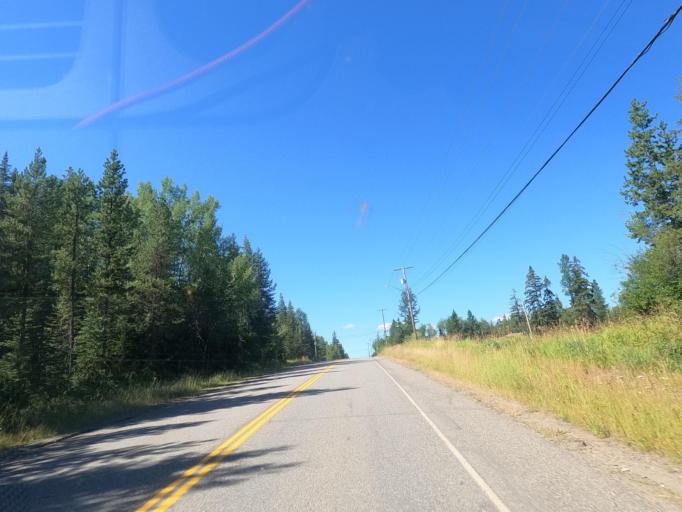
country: CA
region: British Columbia
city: Quesnel
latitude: 53.0293
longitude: -122.4190
